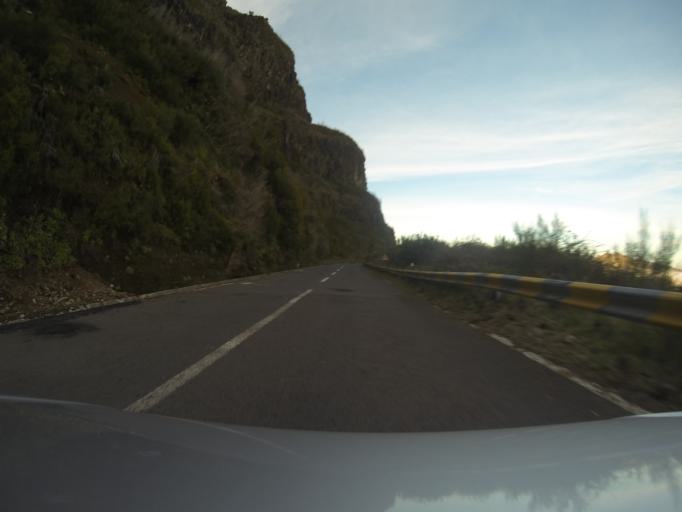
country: PT
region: Madeira
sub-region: Sao Vicente
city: Sao Vicente
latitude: 32.7429
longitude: -17.0444
